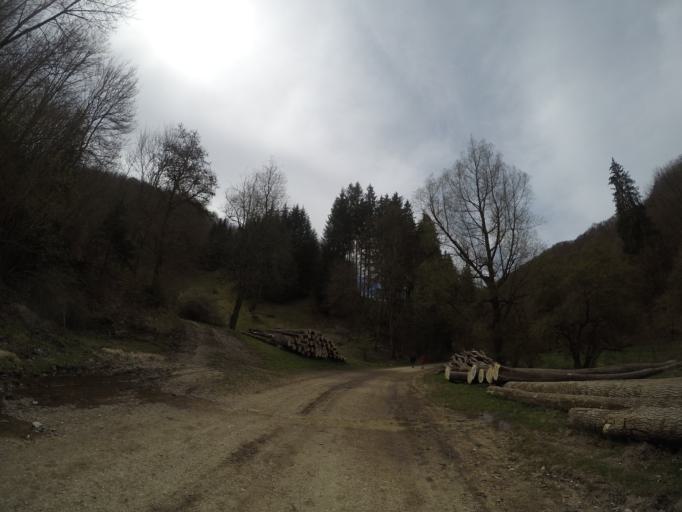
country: DE
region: Baden-Wuerttemberg
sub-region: Regierungsbezirk Stuttgart
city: Wiesensteig
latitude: 48.5522
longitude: 9.6035
